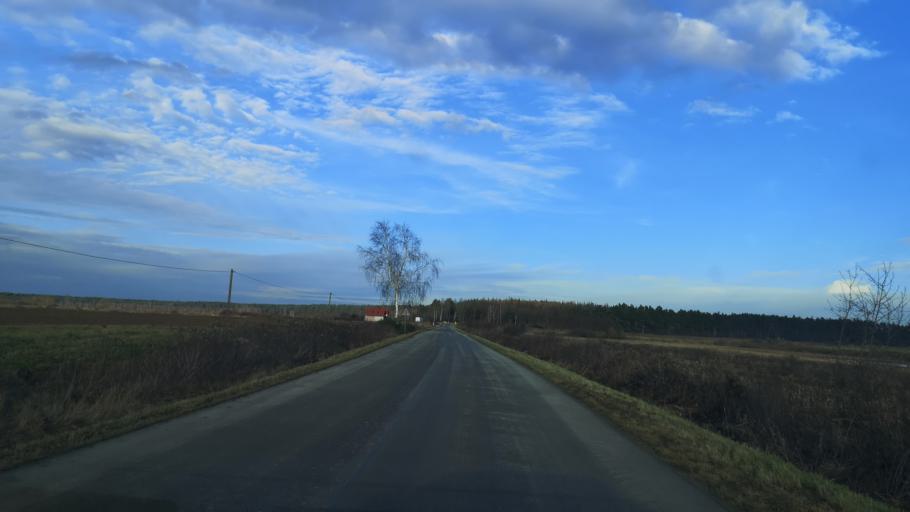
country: PL
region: Subcarpathian Voivodeship
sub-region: Powiat lezajski
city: Piskorowice
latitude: 50.2453
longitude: 22.5463
